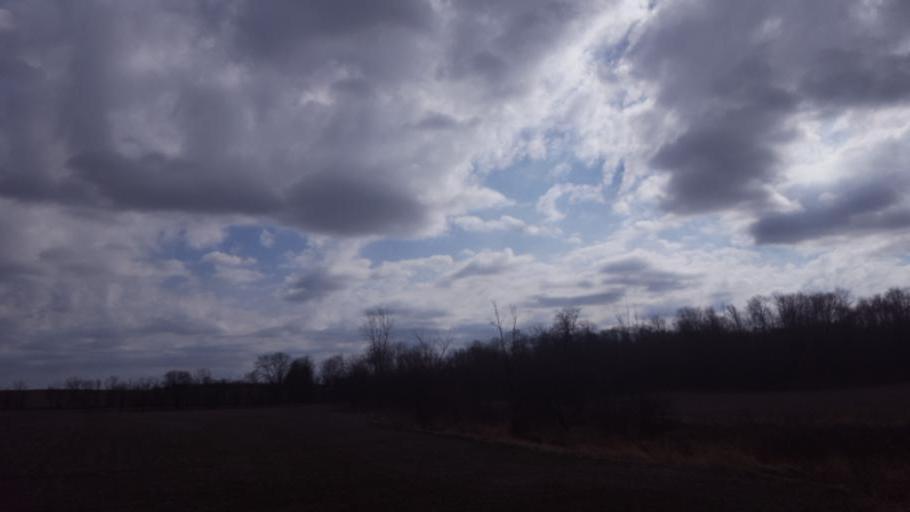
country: US
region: Ohio
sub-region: Knox County
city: Fredericktown
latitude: 40.5190
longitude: -82.6430
